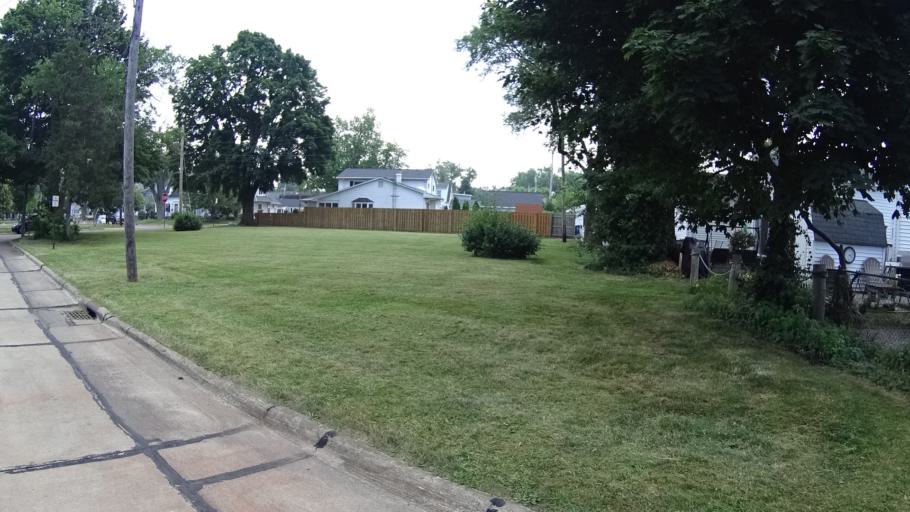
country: US
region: Ohio
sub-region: Erie County
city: Huron
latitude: 41.3946
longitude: -82.5425
